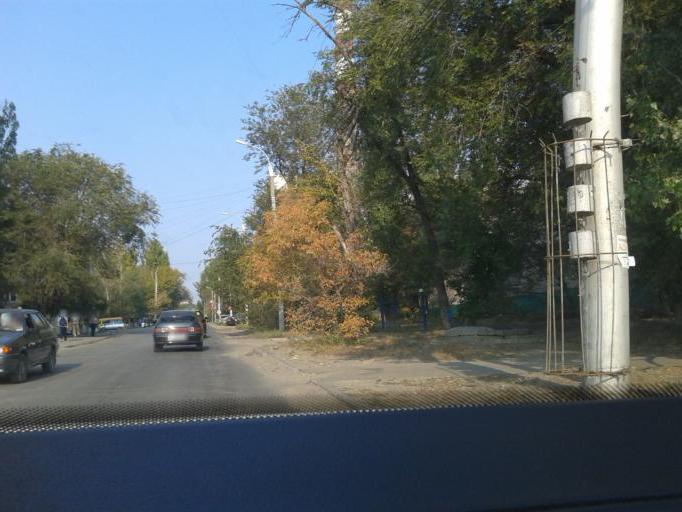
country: RU
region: Volgograd
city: Volgograd
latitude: 48.6154
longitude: 44.4226
